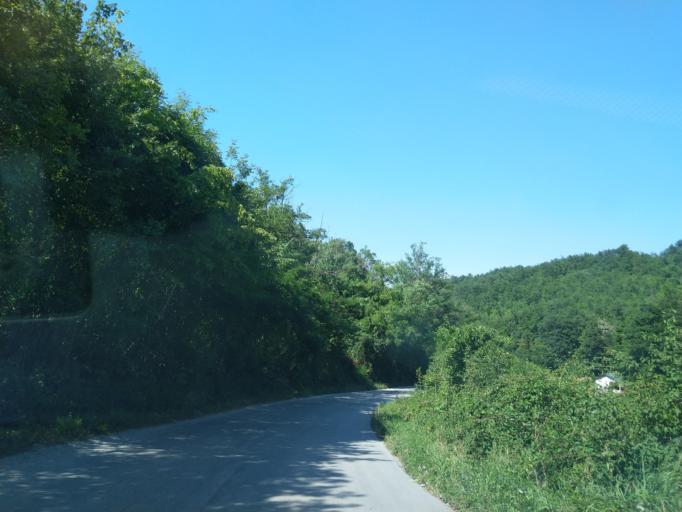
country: RS
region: Central Serbia
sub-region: Zlatiborski Okrug
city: Uzice
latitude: 43.8207
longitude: 19.8575
